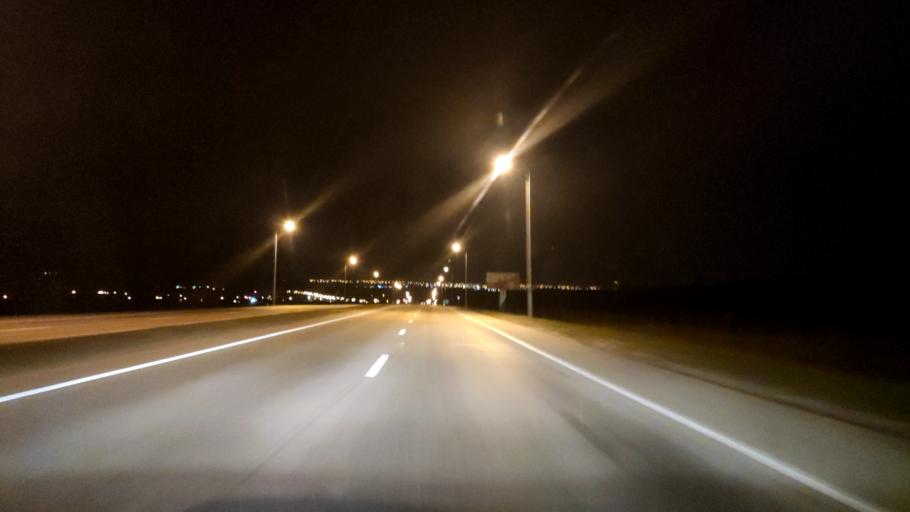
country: RU
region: Belgorod
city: Staryy Oskol
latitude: 51.3391
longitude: 37.7815
